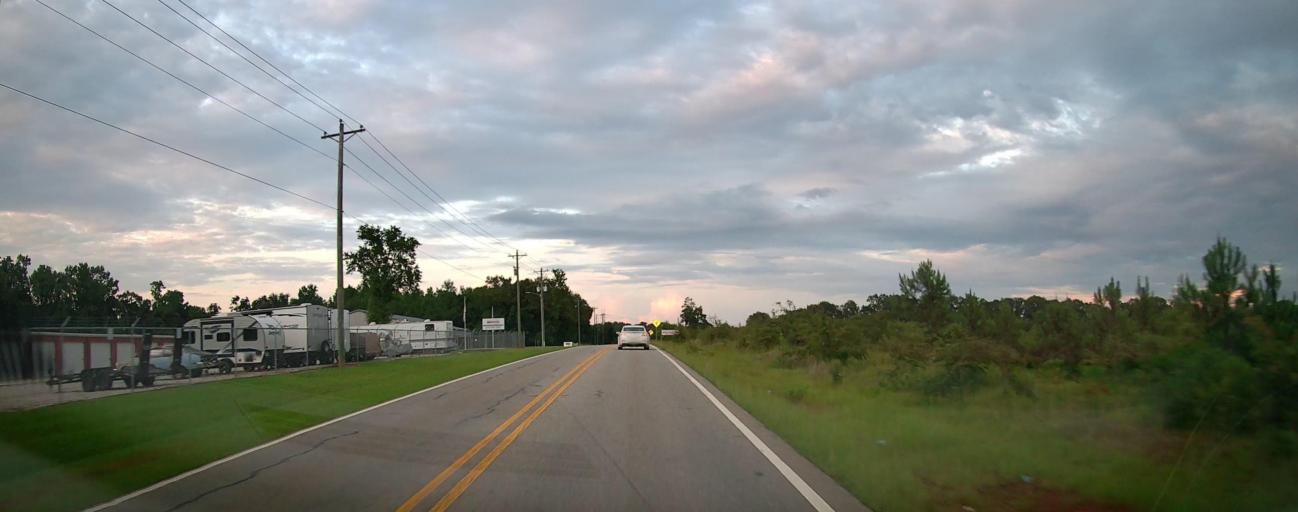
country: US
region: Georgia
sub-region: Peach County
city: Byron
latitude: 32.6169
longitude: -83.7354
